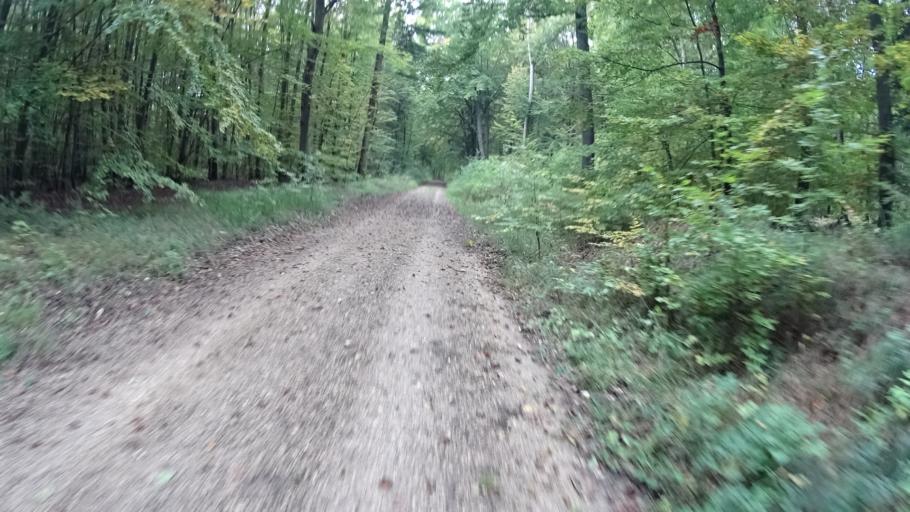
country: DE
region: Bavaria
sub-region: Upper Bavaria
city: Walting
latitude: 48.9039
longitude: 11.3209
